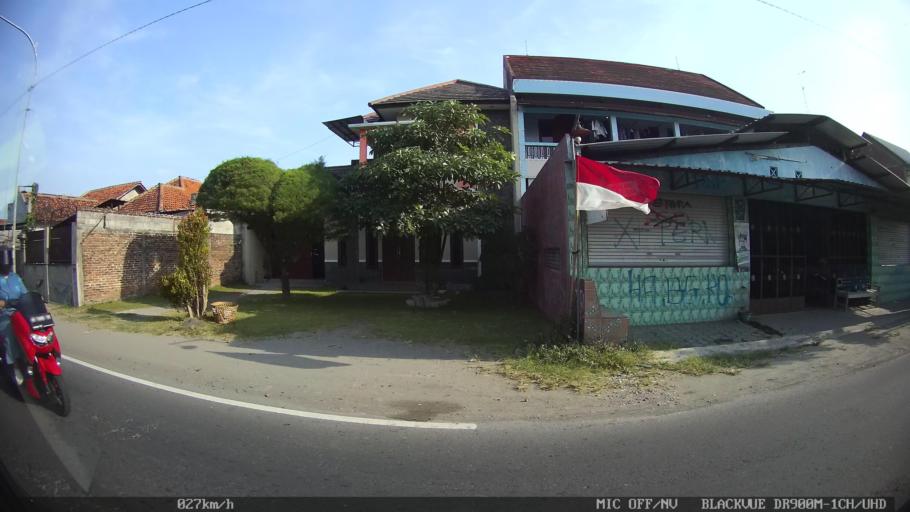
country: ID
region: Daerah Istimewa Yogyakarta
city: Bantul
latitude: -7.8770
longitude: 110.3226
